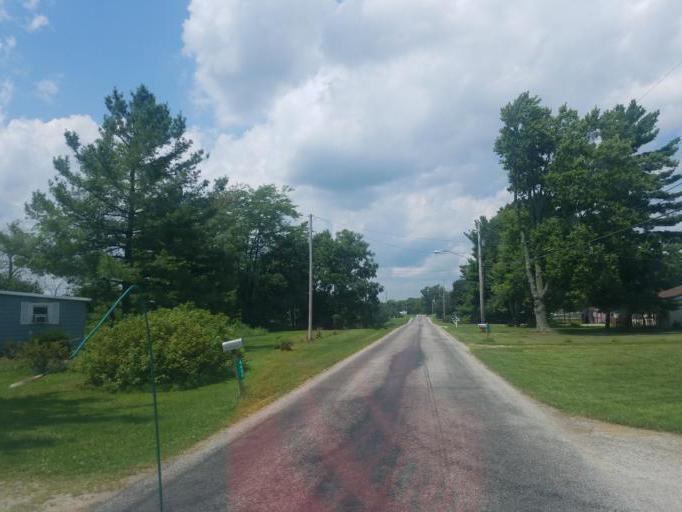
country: US
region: Ohio
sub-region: Crawford County
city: Galion
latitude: 40.6692
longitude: -82.8492
